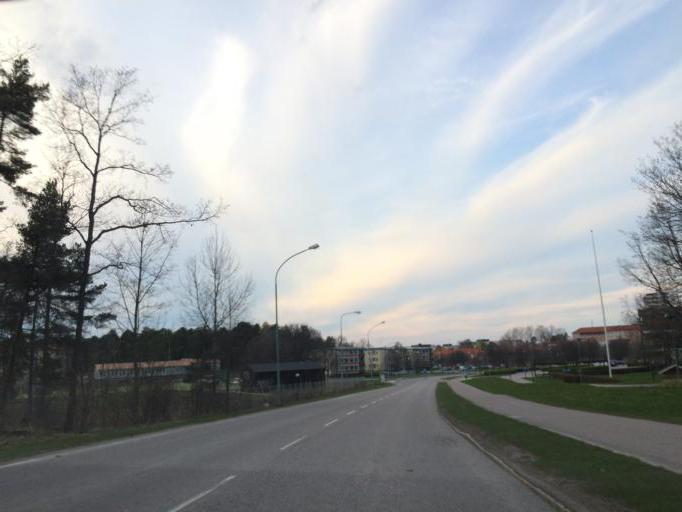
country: SE
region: Soedermanland
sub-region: Eskilstuna Kommun
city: Eskilstuna
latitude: 59.3573
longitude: 16.5312
